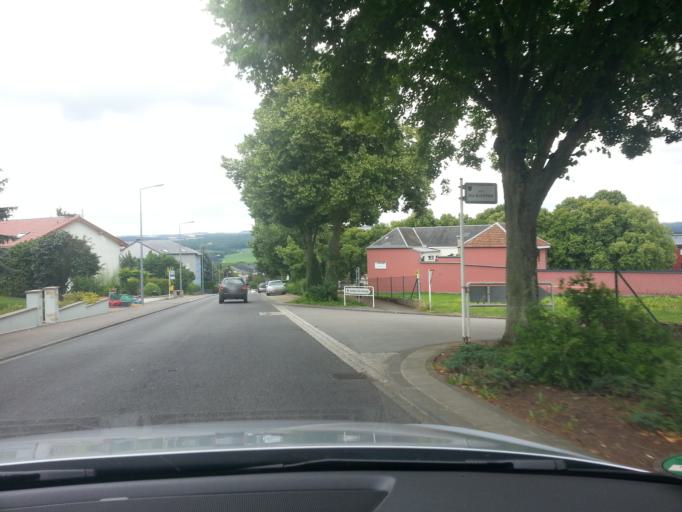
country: LU
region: Grevenmacher
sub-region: Canton de Remich
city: Remich
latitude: 49.5464
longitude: 6.3573
